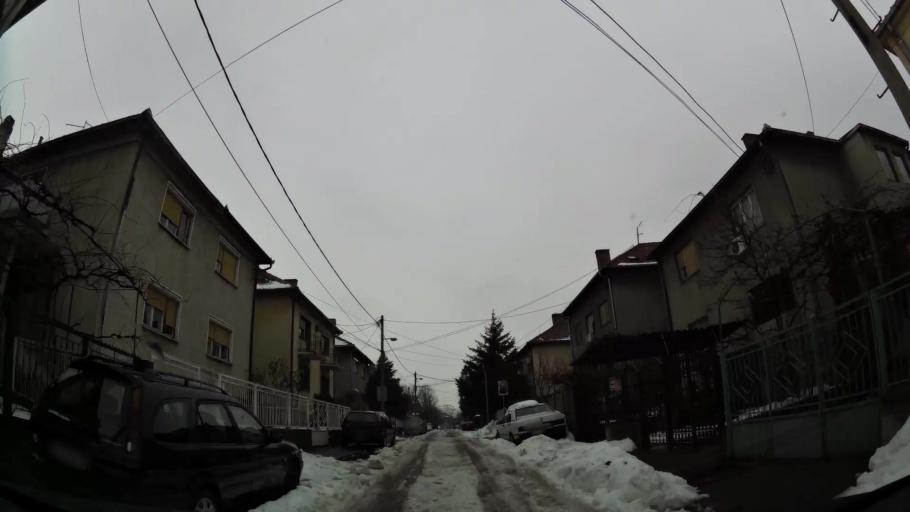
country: RS
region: Central Serbia
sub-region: Belgrade
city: Zemun
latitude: 44.8410
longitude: 20.3715
